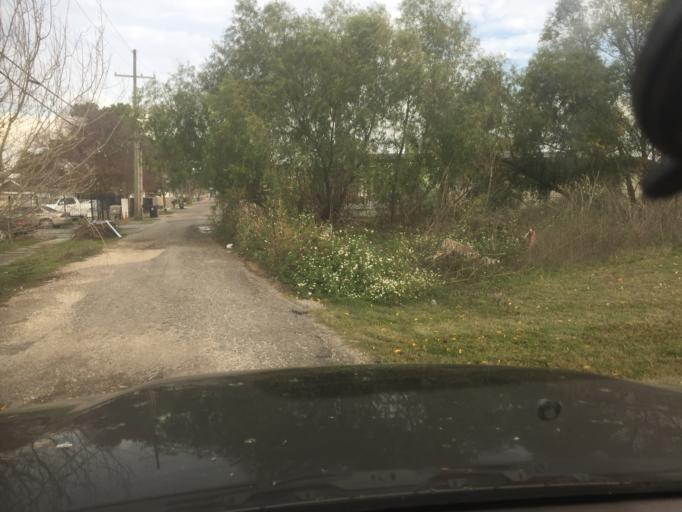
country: US
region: Louisiana
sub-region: Orleans Parish
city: New Orleans
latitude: 29.9935
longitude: -90.0826
